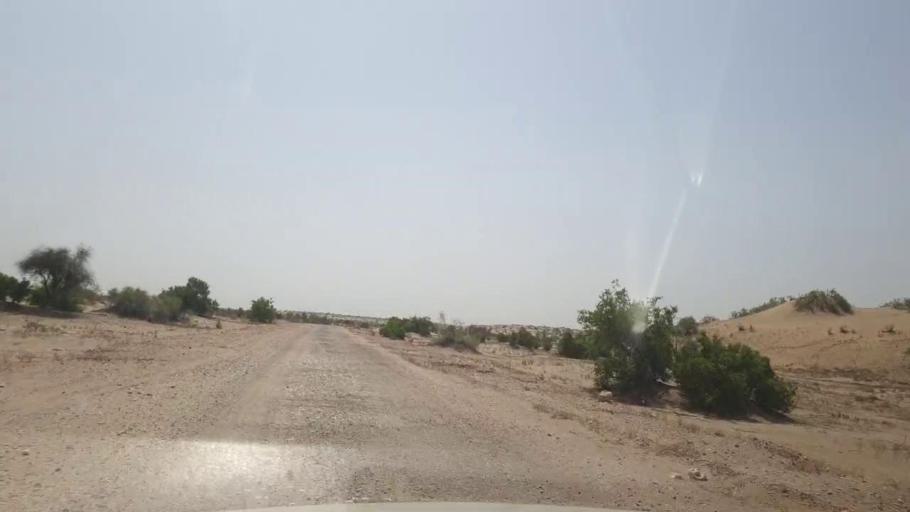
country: PK
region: Sindh
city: Khanpur
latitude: 27.4085
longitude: 69.3219
